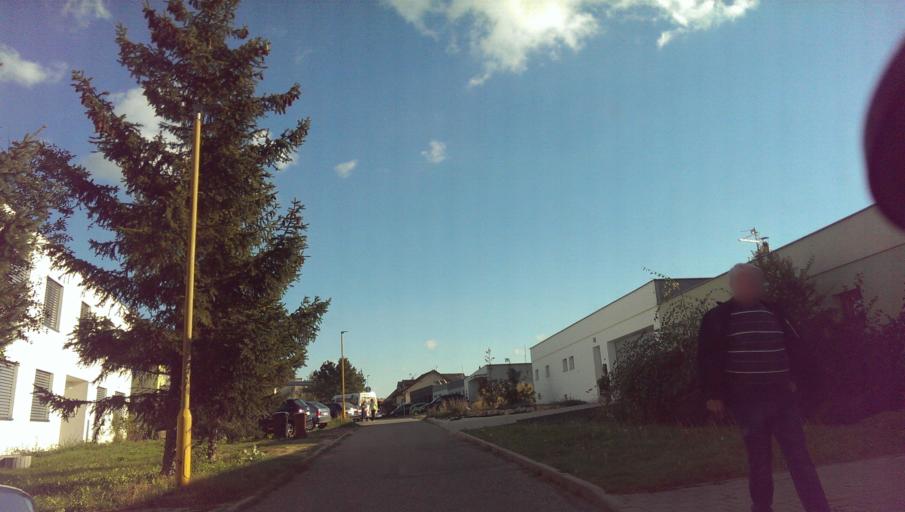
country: CZ
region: Zlin
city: Kunovice
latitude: 49.0621
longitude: 17.4769
